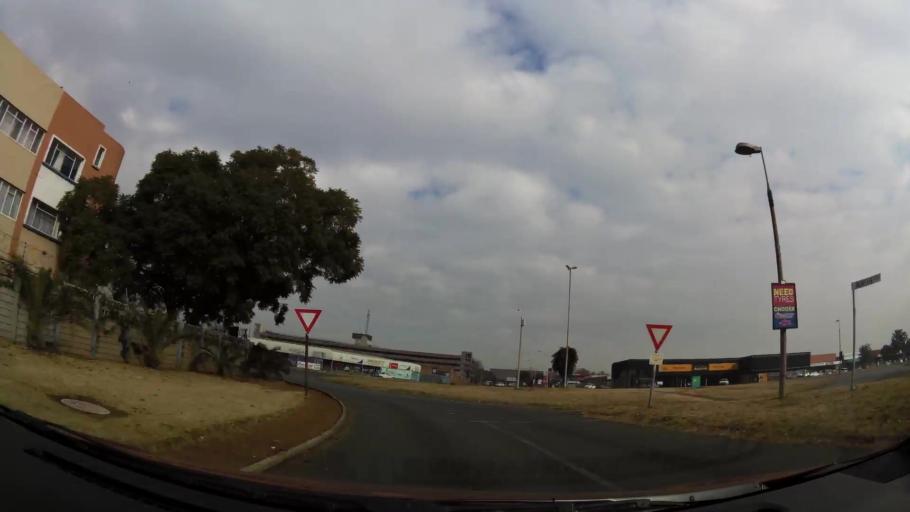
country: ZA
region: Gauteng
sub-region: Sedibeng District Municipality
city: Vanderbijlpark
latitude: -26.6976
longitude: 27.8408
